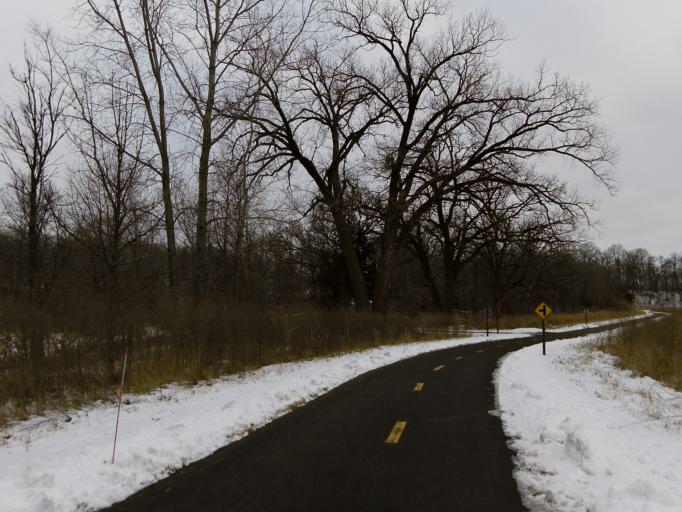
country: US
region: Minnesota
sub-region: Scott County
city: Prior Lake
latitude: 44.7117
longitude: -93.4669
